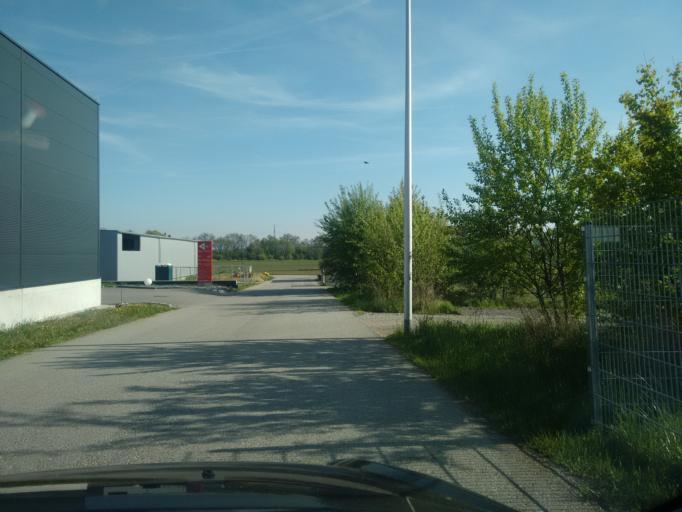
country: AT
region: Upper Austria
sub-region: Wels-Land
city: Holzhausen
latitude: 48.2084
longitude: 14.0884
